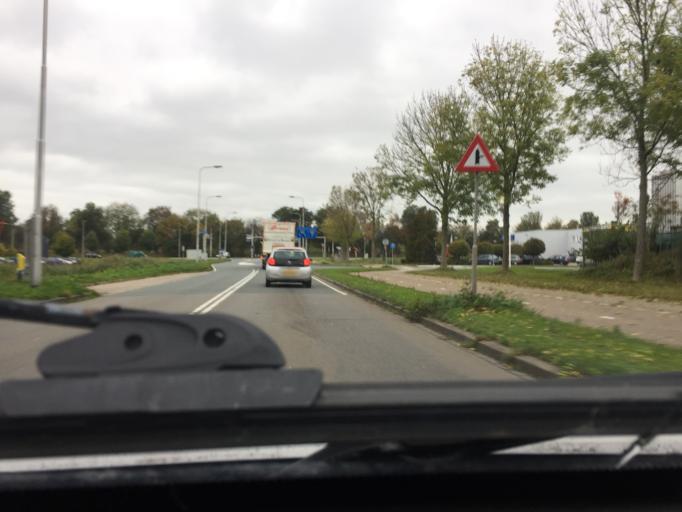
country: NL
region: North Holland
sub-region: Gemeente Heerhugowaard
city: Heerhugowaard
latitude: 52.6853
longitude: 4.8292
